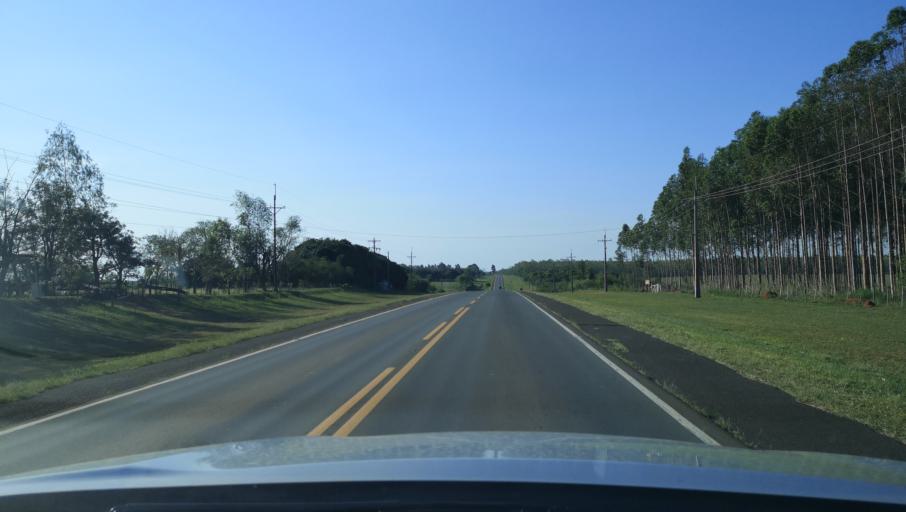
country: PY
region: Misiones
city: Santa Maria
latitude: -26.7731
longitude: -57.0300
